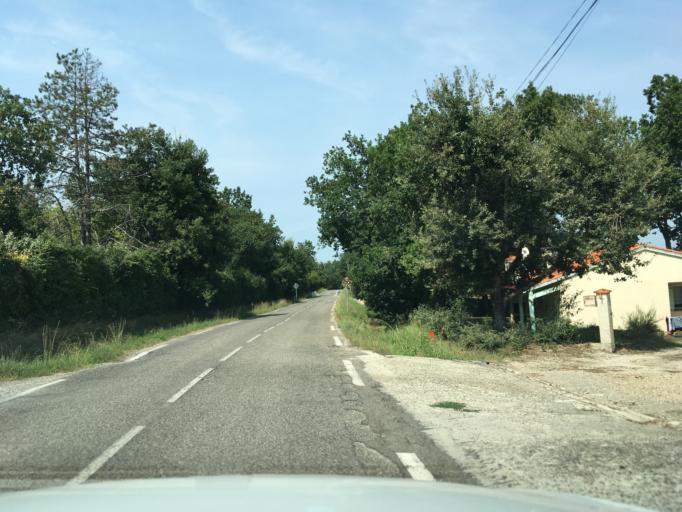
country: FR
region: Midi-Pyrenees
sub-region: Departement du Tarn-et-Garonne
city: Corbarieu
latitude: 43.9715
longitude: 1.3703
